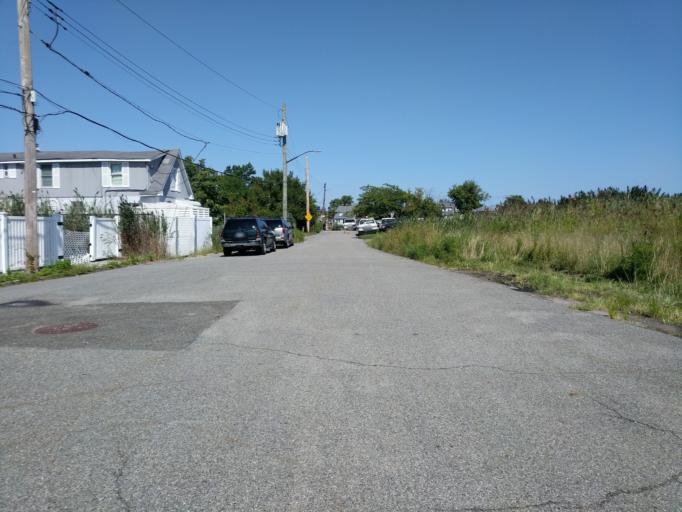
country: US
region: New York
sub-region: Queens County
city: Borough of Queens
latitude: 40.6568
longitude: -73.8319
